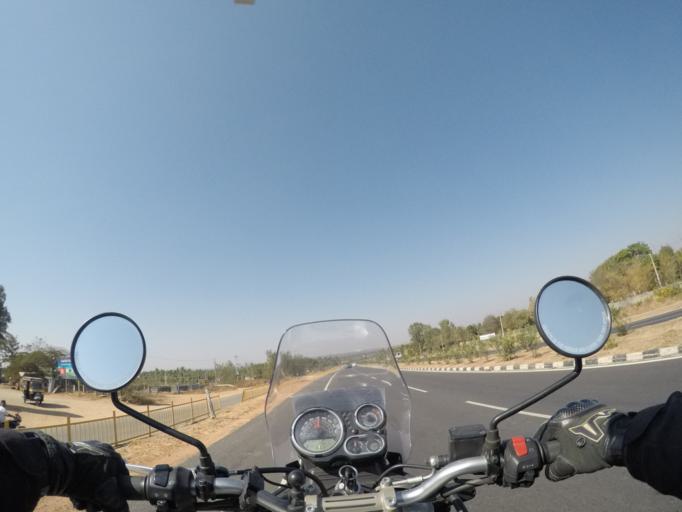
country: IN
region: Karnataka
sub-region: Mandya
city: Belluru
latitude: 12.9796
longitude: 76.8573
